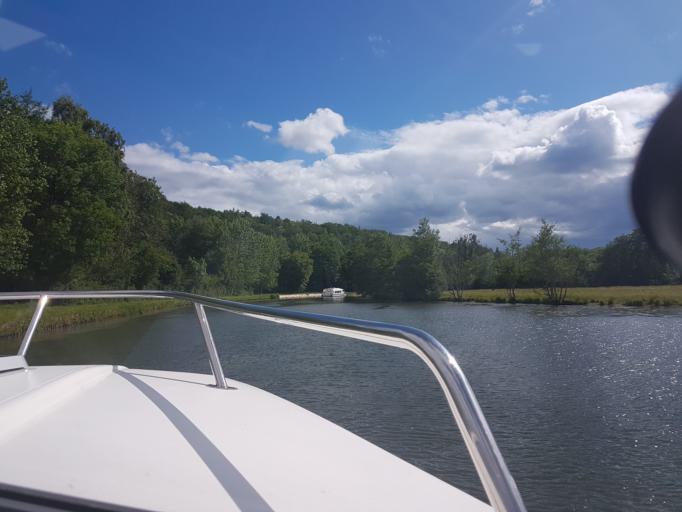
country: FR
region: Bourgogne
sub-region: Departement de l'Yonne
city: Vermenton
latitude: 47.5614
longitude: 3.6508
